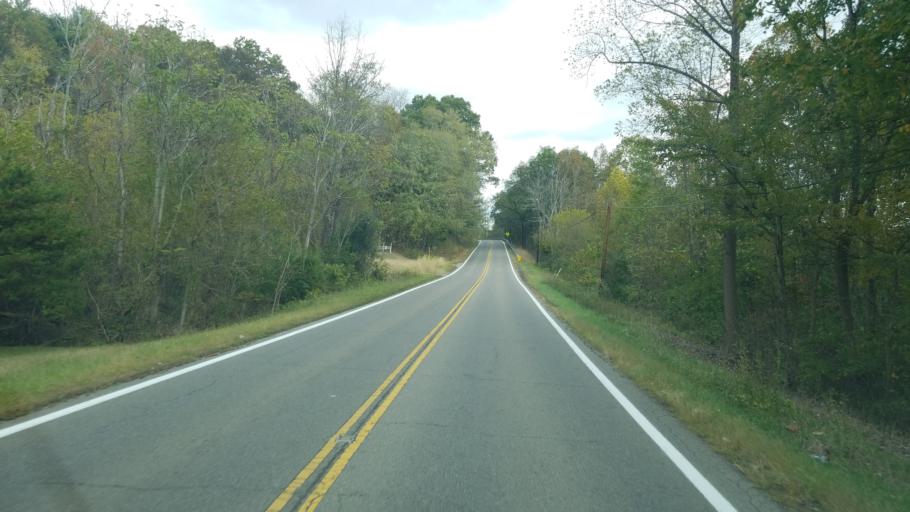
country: US
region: Ohio
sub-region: Jackson County
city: Wellston
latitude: 39.1148
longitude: -82.5744
